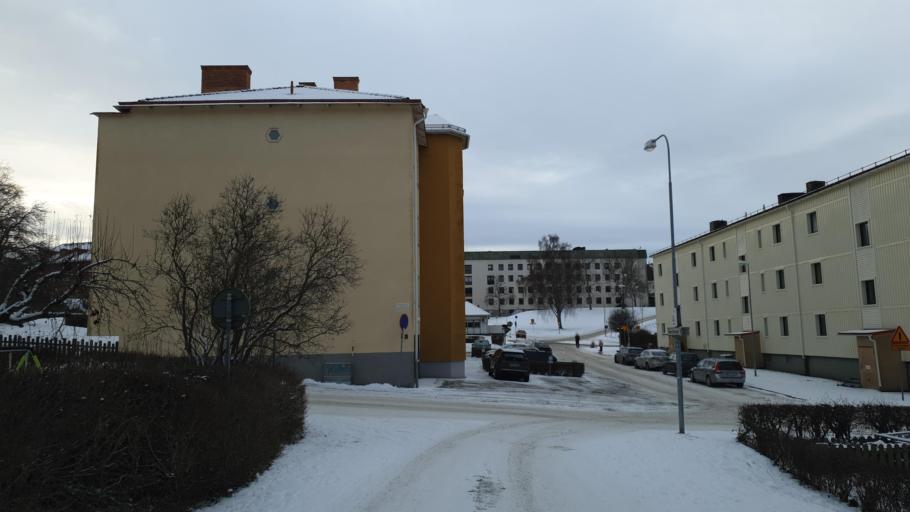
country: SE
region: Gaevleborg
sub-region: Soderhamns Kommun
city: Soderhamn
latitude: 61.2994
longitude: 17.0586
